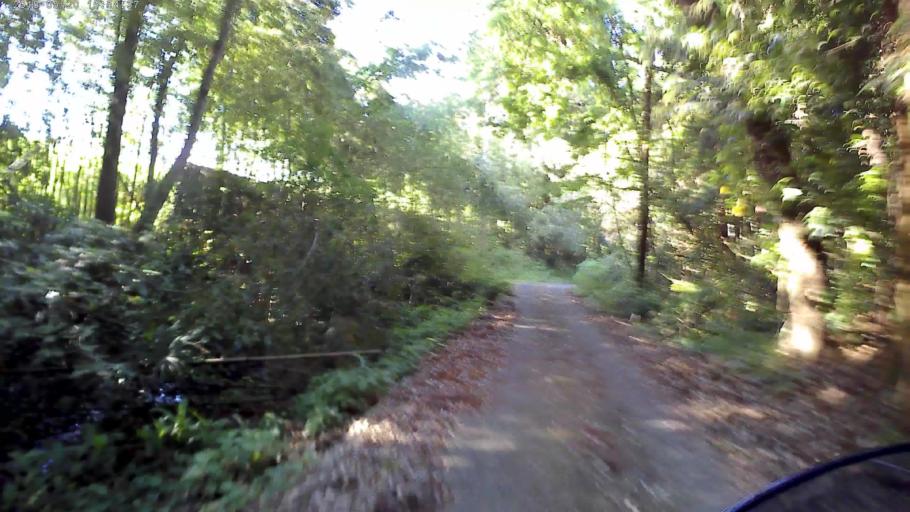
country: JP
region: Kanagawa
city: Hadano
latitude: 35.3284
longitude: 139.2038
